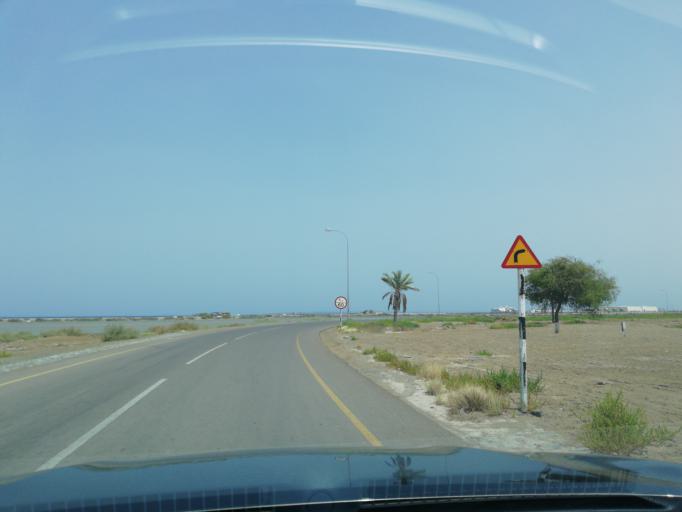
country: OM
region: Al Batinah
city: Shinas
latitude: 24.7537
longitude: 56.4661
